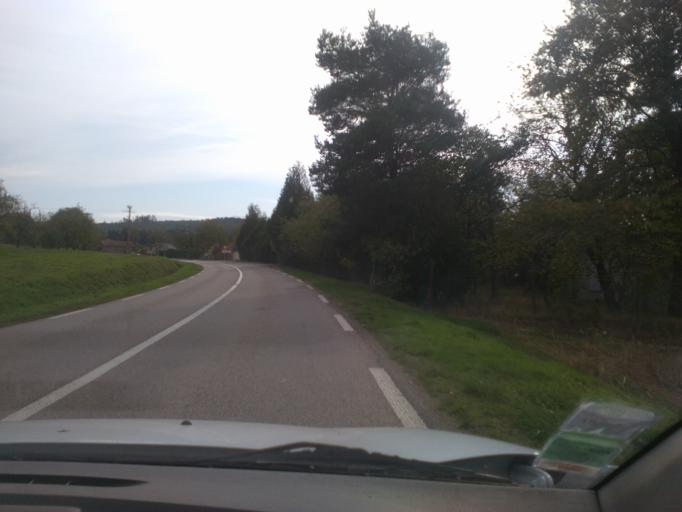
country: FR
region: Lorraine
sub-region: Departement des Vosges
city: Jeanmenil
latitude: 48.3282
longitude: 6.7059
